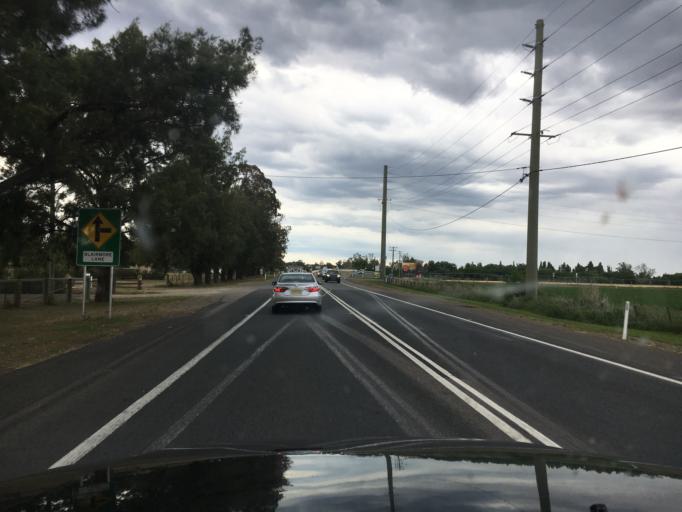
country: AU
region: New South Wales
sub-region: Muswellbrook
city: Muswellbrook
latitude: -32.1529
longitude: 150.8846
